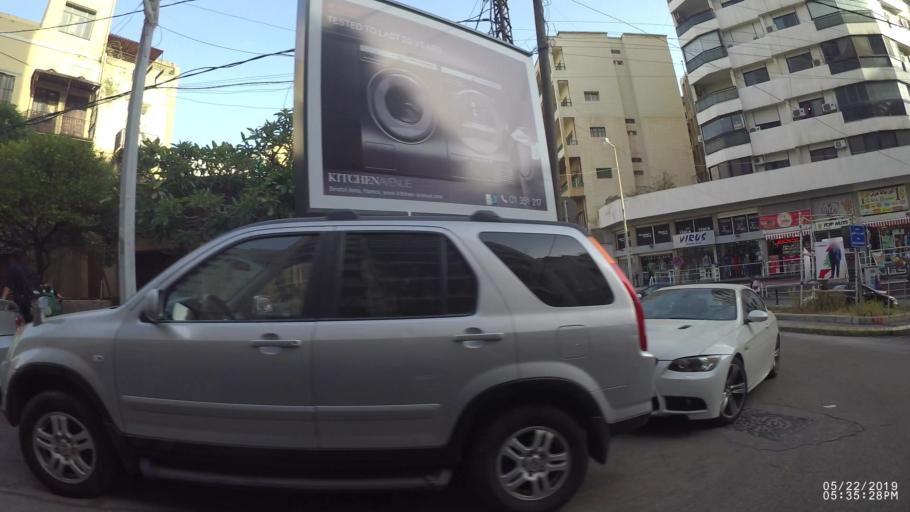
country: LB
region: Beyrouth
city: Ra's Bayrut
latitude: 33.8972
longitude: 35.4740
